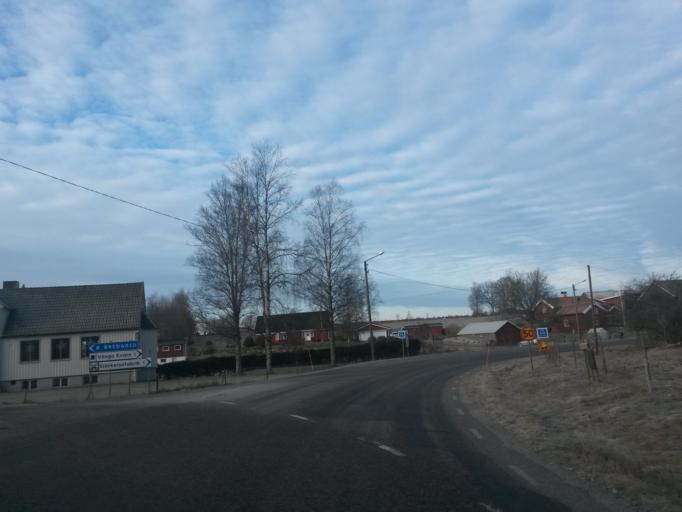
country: SE
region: Vaestra Goetaland
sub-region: Boras Kommun
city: Boras
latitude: 57.8578
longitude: 12.9282
